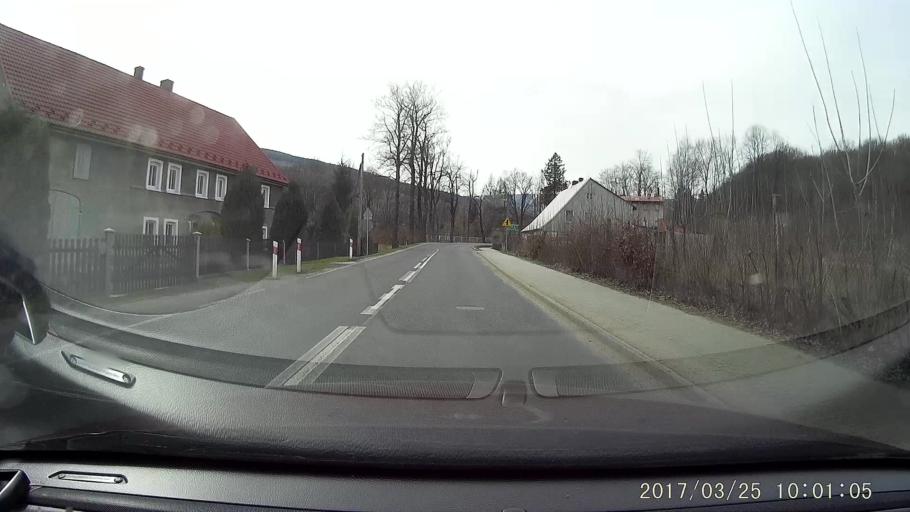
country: PL
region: Lower Silesian Voivodeship
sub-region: Powiat lubanski
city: Swieradow-Zdroj
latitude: 50.9291
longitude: 15.3541
